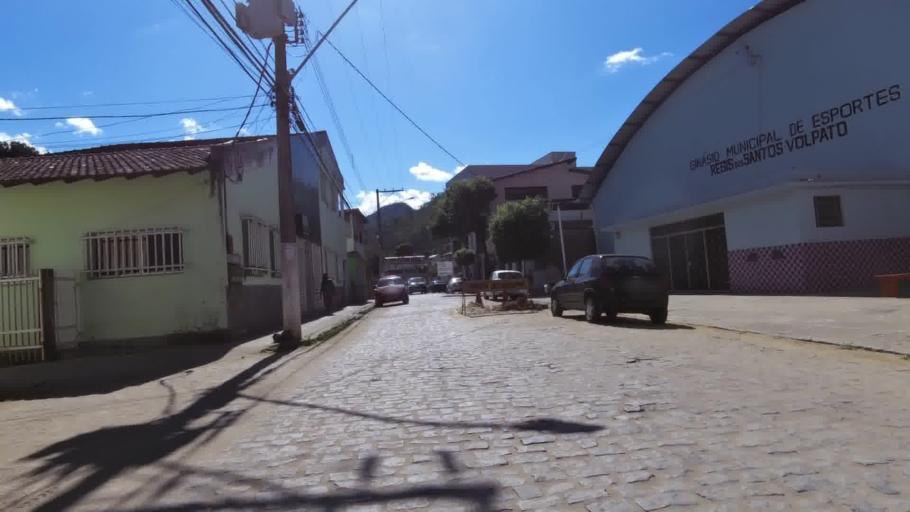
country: BR
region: Espirito Santo
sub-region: Rio Novo Do Sul
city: Rio Novo do Sul
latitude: -20.8642
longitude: -40.9327
